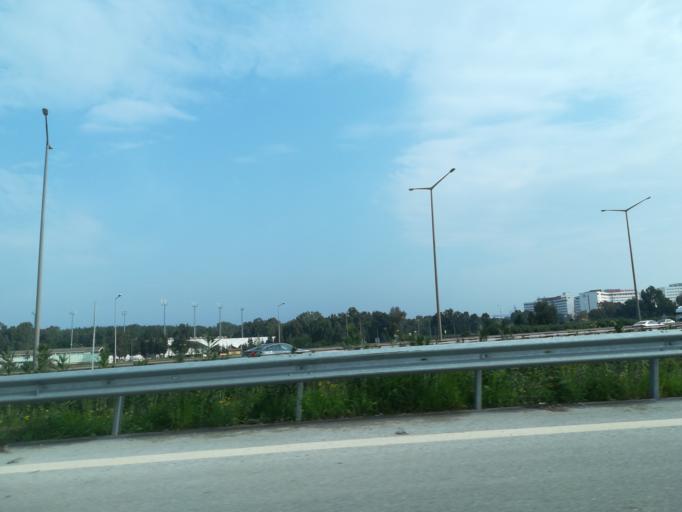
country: TR
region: Adana
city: Adana
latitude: 37.0230
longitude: 35.3401
